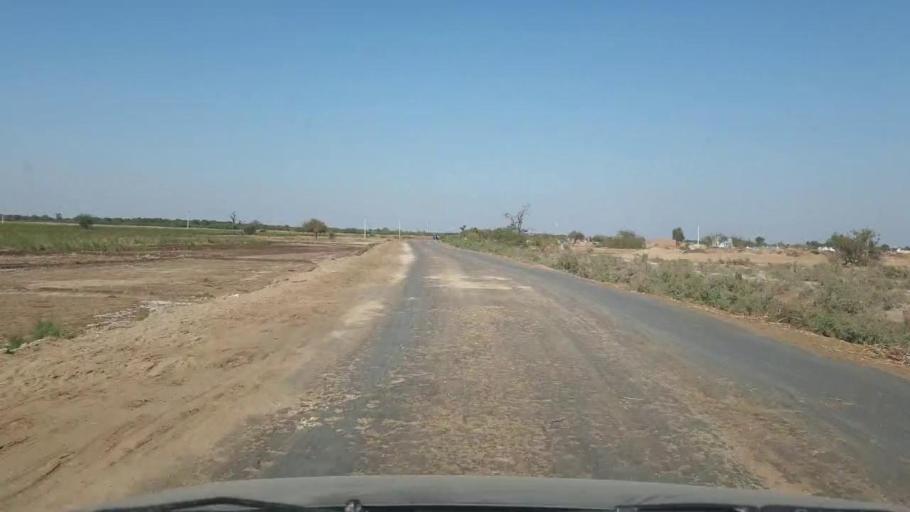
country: PK
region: Sindh
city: Samaro
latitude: 25.3234
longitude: 69.3018
